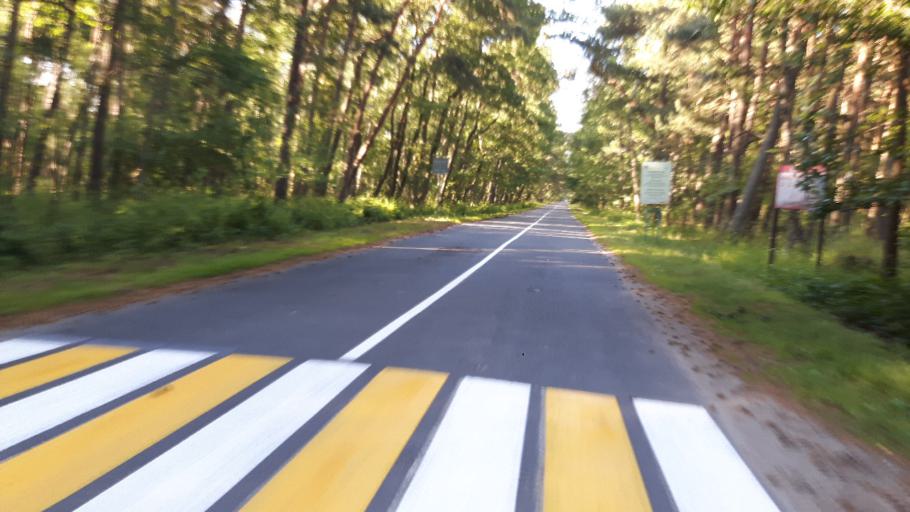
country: LT
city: Nida
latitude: 55.2484
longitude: 20.9241
